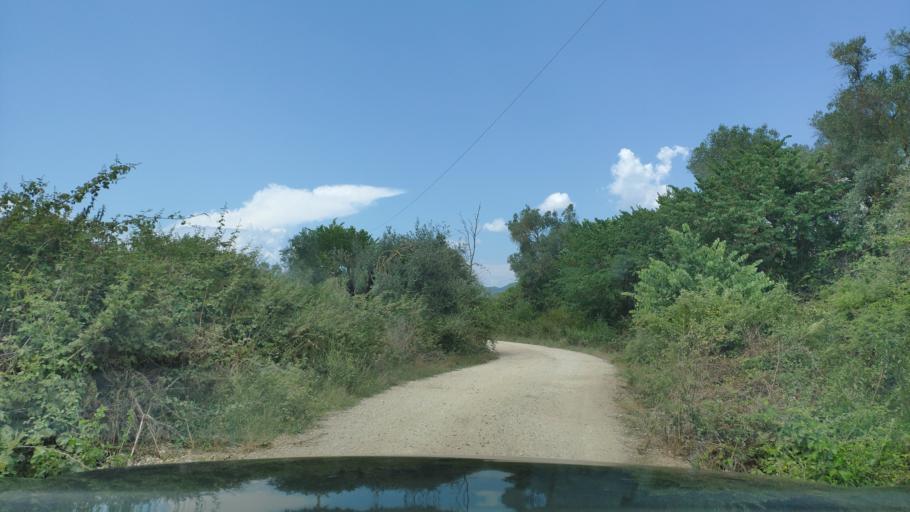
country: GR
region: West Greece
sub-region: Nomos Aitolias kai Akarnanias
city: Menidi
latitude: 39.0608
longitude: 21.0944
